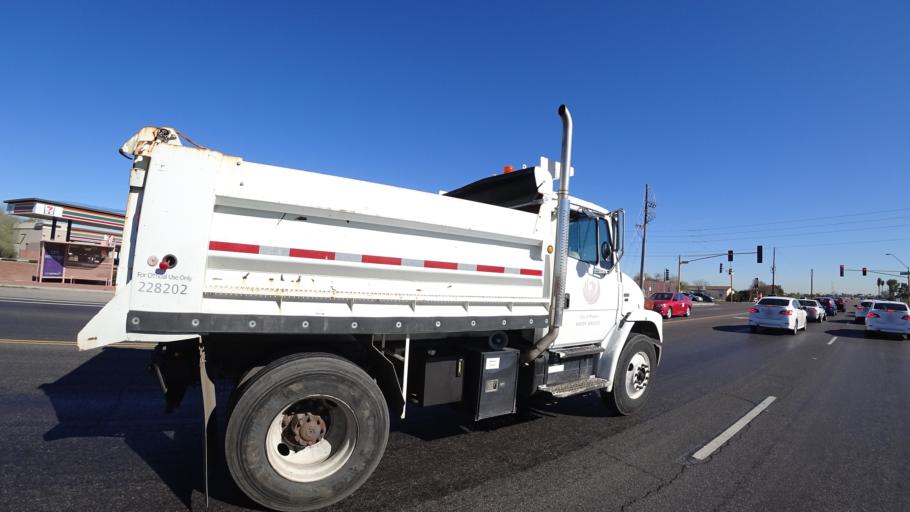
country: US
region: Arizona
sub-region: Maricopa County
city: Tolleson
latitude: 33.4937
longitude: -112.2732
